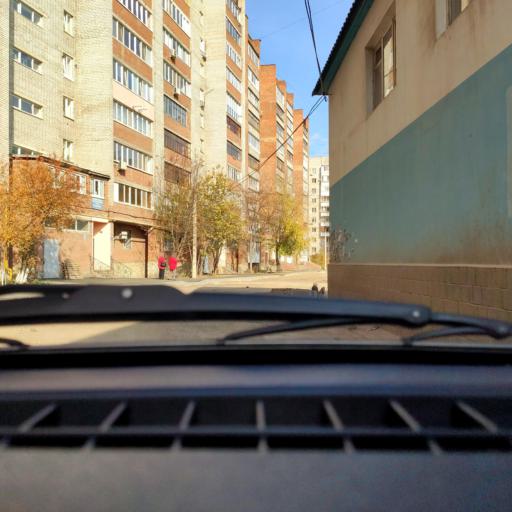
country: RU
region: Bashkortostan
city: Ufa
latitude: 54.7444
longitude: 55.9996
